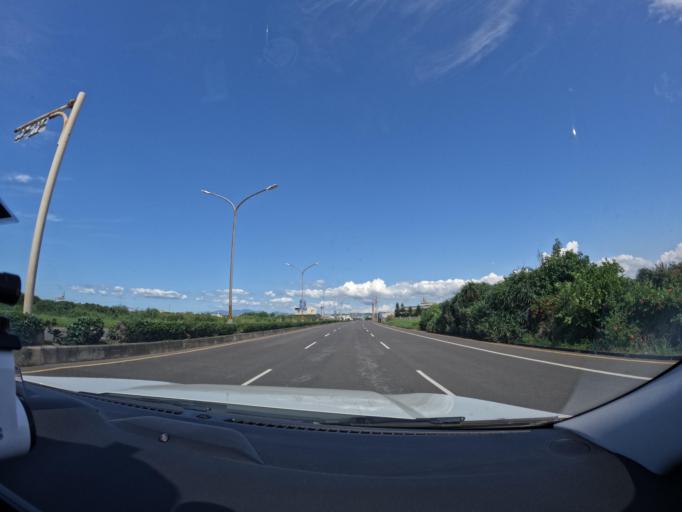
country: TW
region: Taiwan
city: Taoyuan City
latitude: 25.1076
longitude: 121.2326
